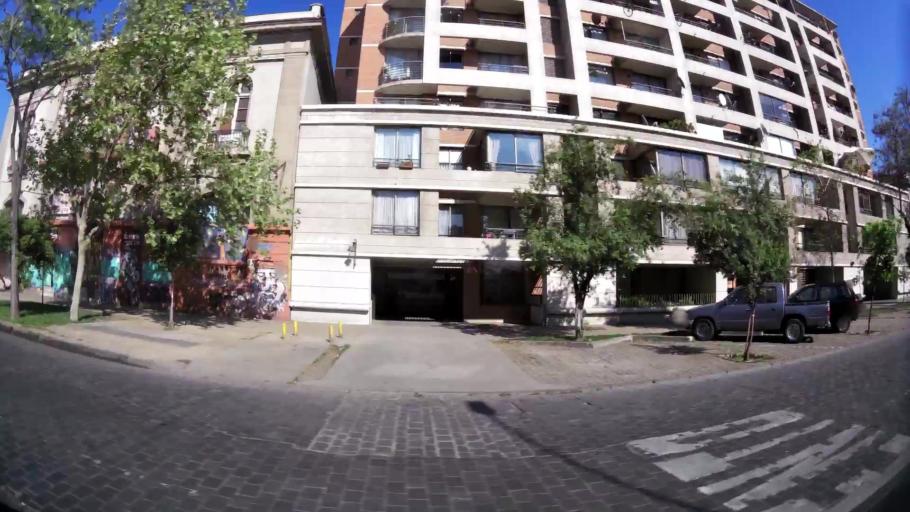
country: CL
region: Santiago Metropolitan
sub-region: Provincia de Santiago
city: Santiago
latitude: -33.4503
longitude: -70.6702
